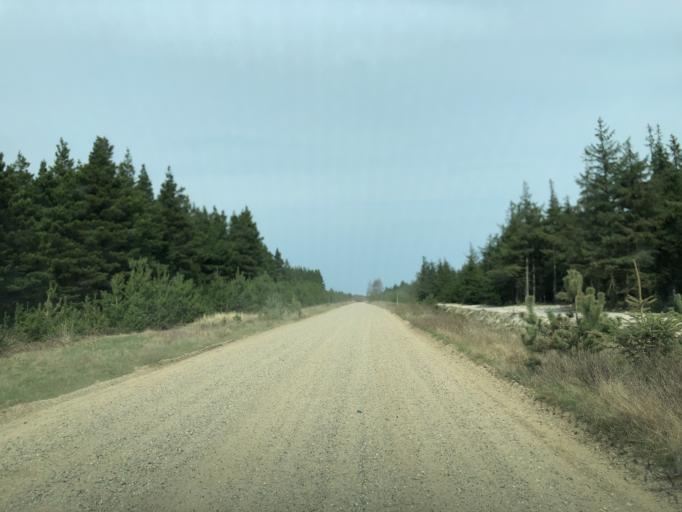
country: DK
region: South Denmark
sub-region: Varde Kommune
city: Oksbol
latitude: 55.6044
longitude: 8.1592
